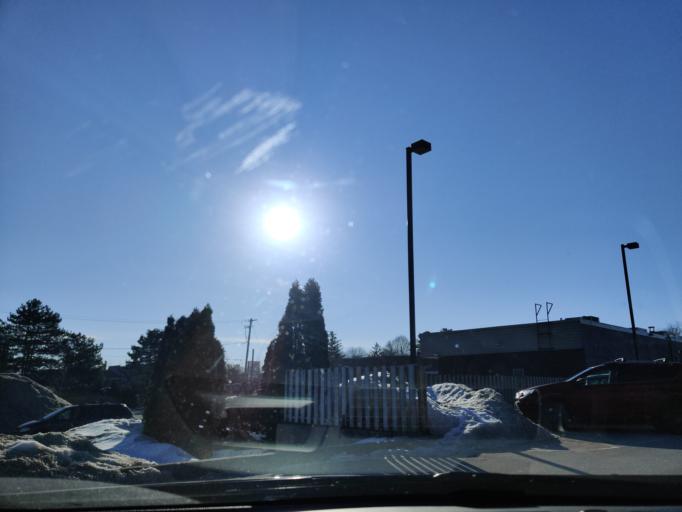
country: CA
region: Ontario
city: Collingwood
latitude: 44.5028
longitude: -80.2261
